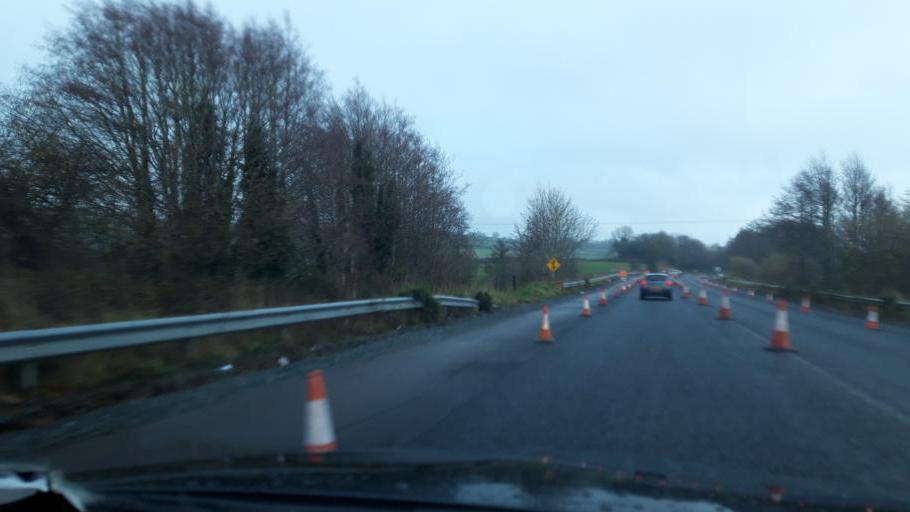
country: IE
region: Ulster
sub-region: County Donegal
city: Raphoe
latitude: 54.9417
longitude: -7.6261
